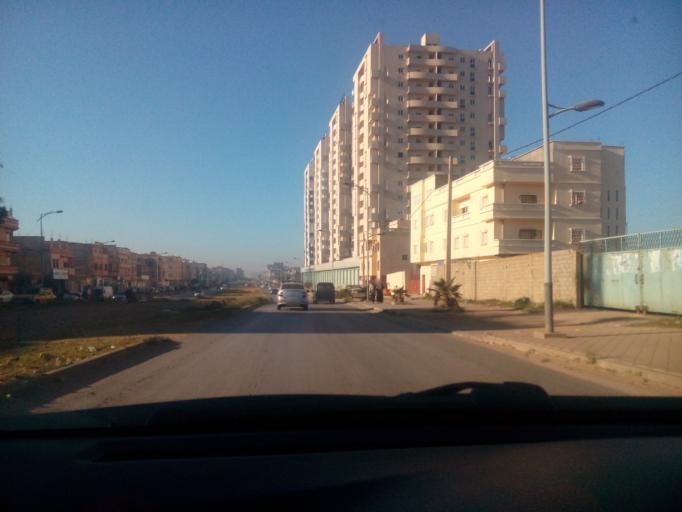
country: DZ
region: Oran
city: Bir el Djir
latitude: 35.7497
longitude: -0.5539
